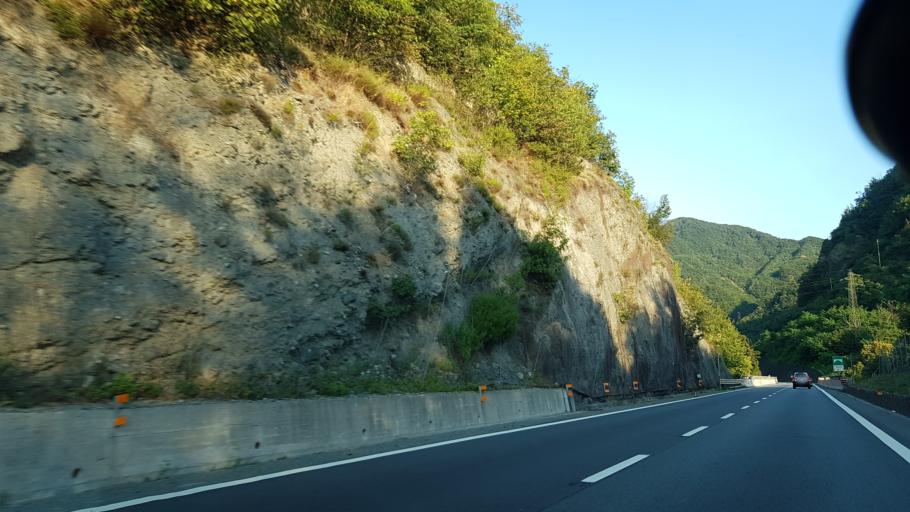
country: IT
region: Piedmont
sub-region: Provincia di Alessandria
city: Arquata Scrivia
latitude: 44.6633
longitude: 8.9132
